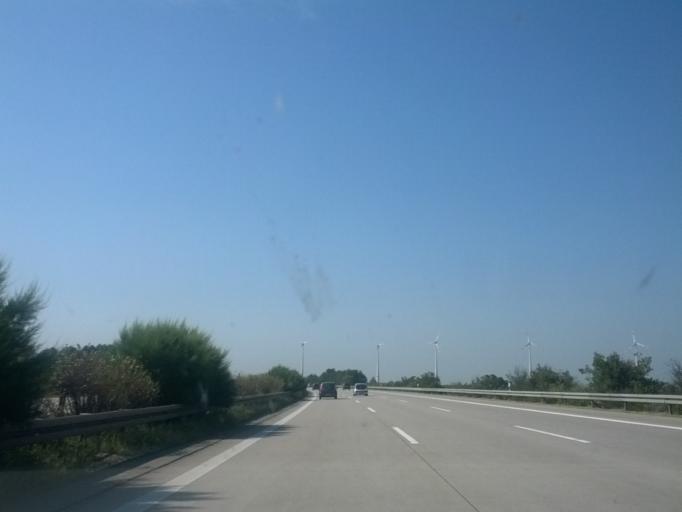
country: DE
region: Brandenburg
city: Borkheide
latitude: 52.1903
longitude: 12.8544
